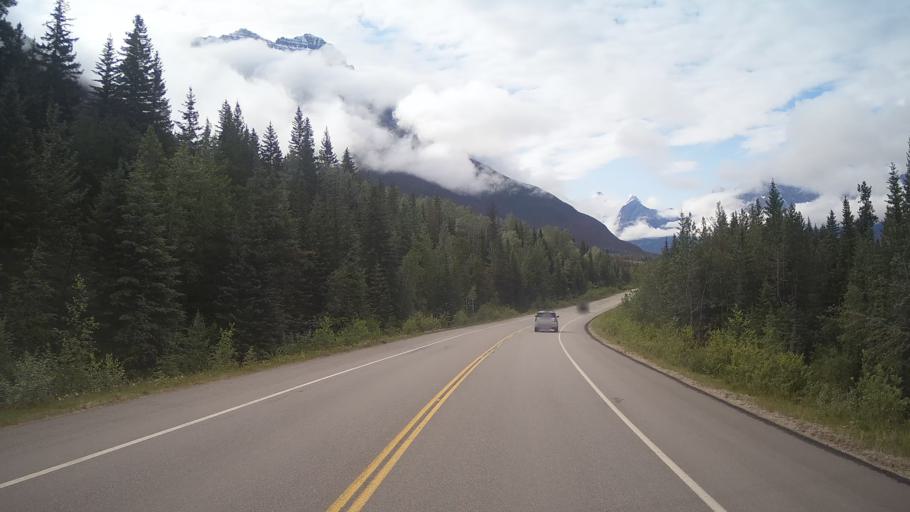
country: CA
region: Alberta
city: Jasper Park Lodge
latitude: 52.6927
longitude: -117.8665
